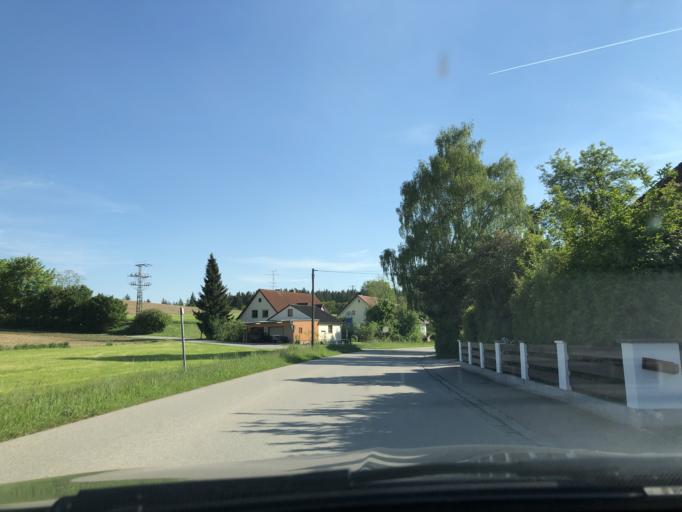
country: DE
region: Bavaria
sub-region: Upper Bavaria
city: Kirchdorf
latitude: 48.4250
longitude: 11.6651
